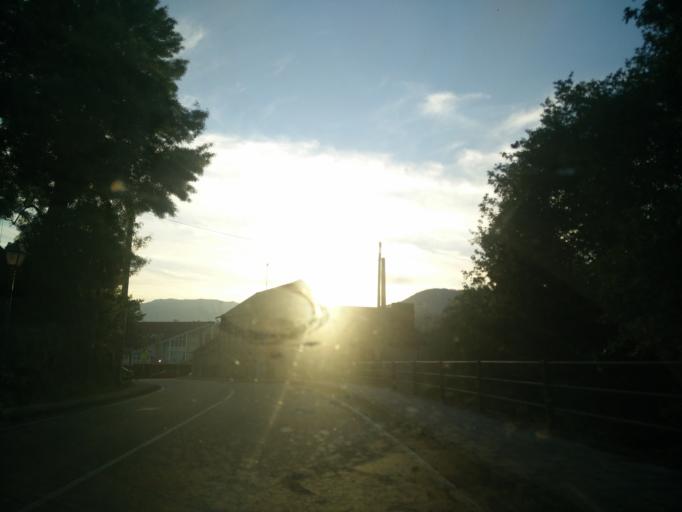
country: ES
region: Galicia
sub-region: Provincia de Pontevedra
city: Mondariz-Balneario
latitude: 42.2272
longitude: -8.4637
